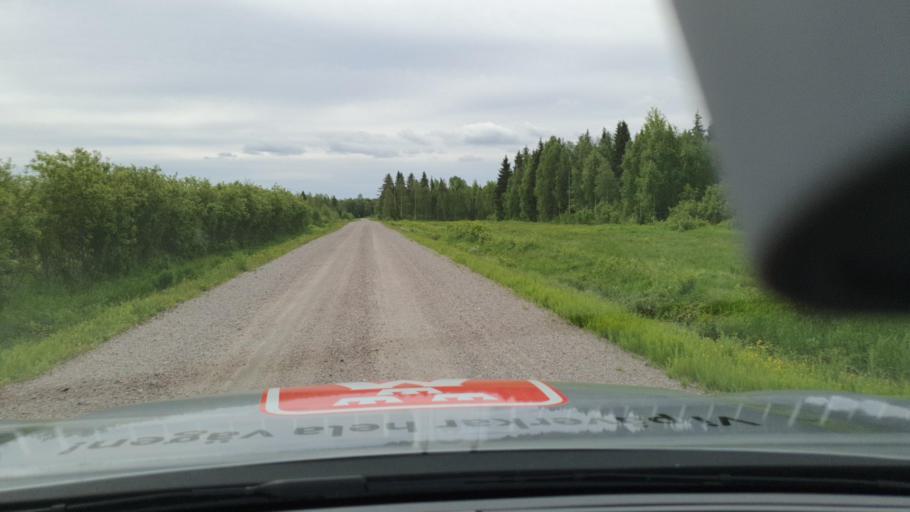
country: SE
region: Norrbotten
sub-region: Kalix Kommun
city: Kalix
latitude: 65.9851
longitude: 23.4587
